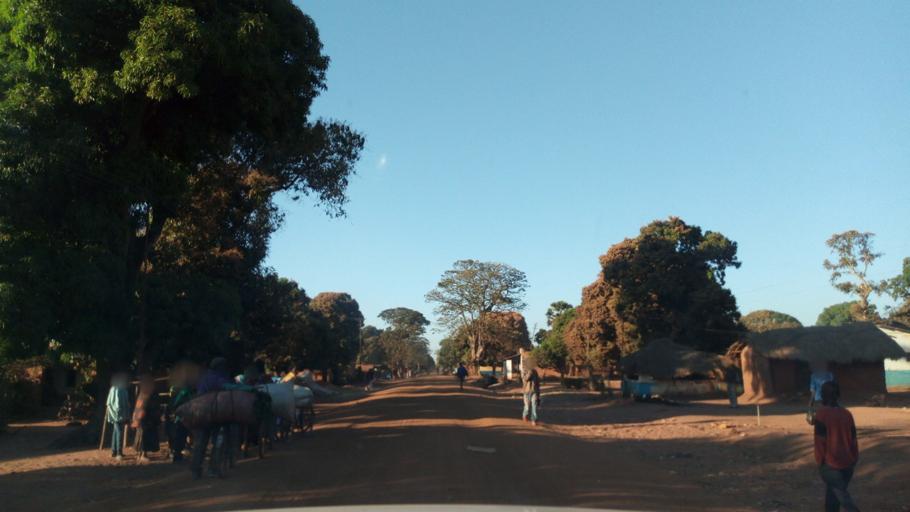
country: ZM
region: Luapula
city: Mwense
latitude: -10.3735
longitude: 28.6140
